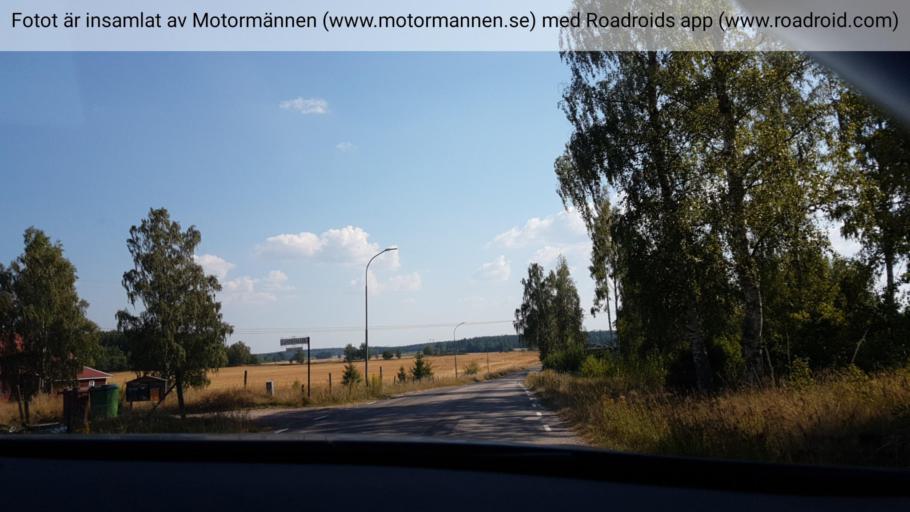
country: SE
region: Vaestra Goetaland
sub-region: Mariestads Kommun
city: Mariestad
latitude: 58.5915
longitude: 13.8625
